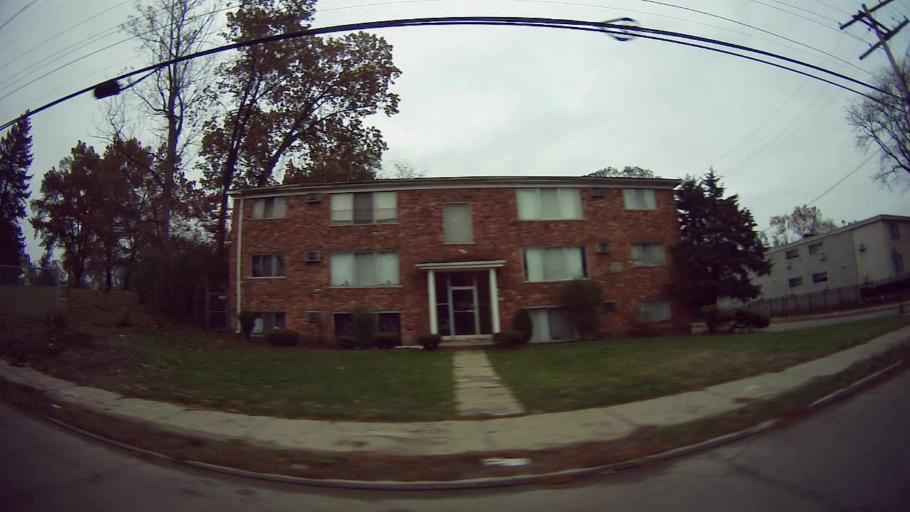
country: US
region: Michigan
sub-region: Wayne County
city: Redford
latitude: 42.4244
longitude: -83.2582
